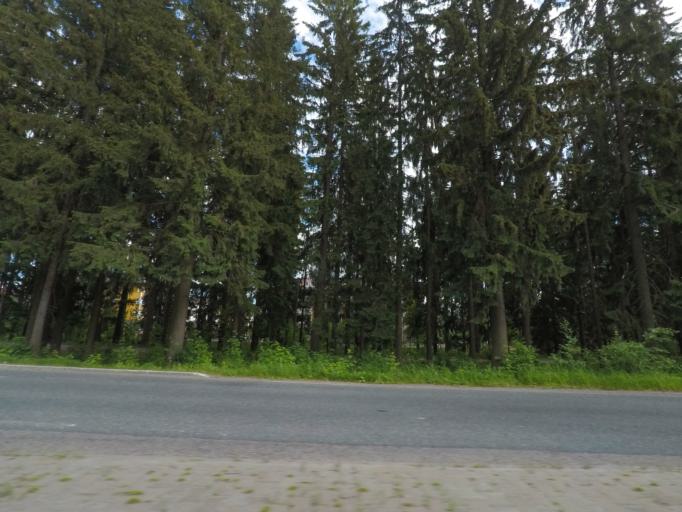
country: FI
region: Paijanne Tavastia
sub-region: Lahti
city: Lahti
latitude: 60.9716
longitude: 25.6324
